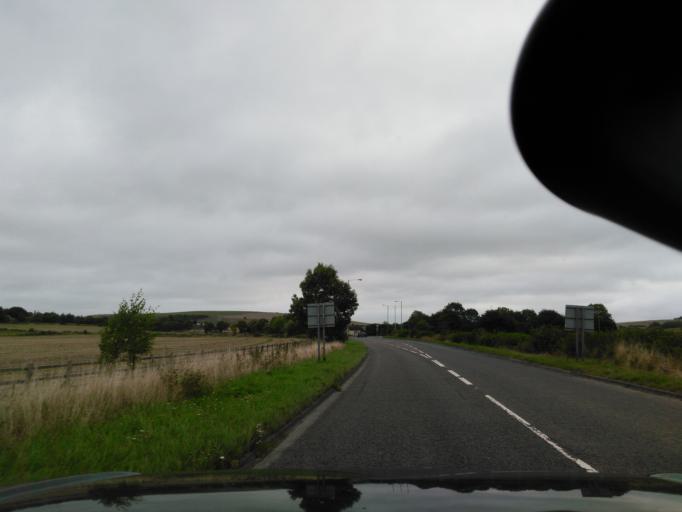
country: GB
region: England
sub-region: Wiltshire
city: Upton Scudamore
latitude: 51.2248
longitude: -2.1899
